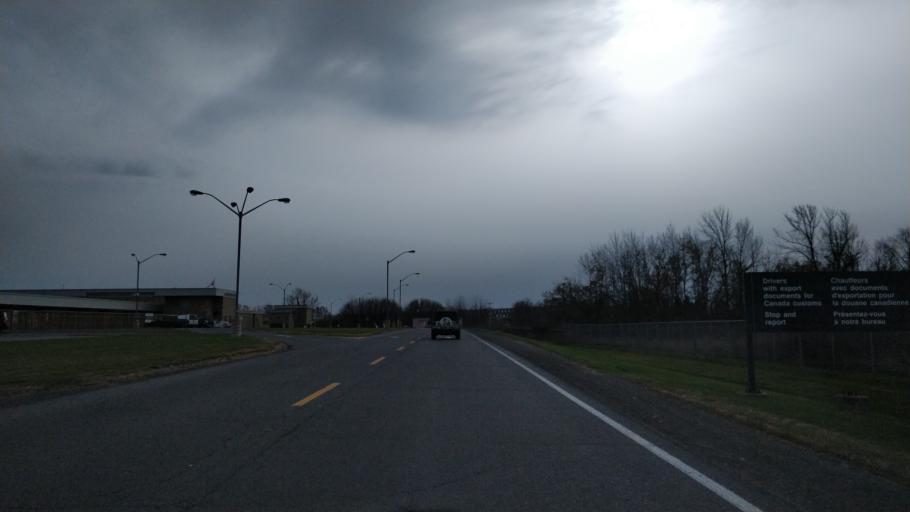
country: CA
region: Ontario
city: Prescott
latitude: 44.7457
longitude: -75.4713
